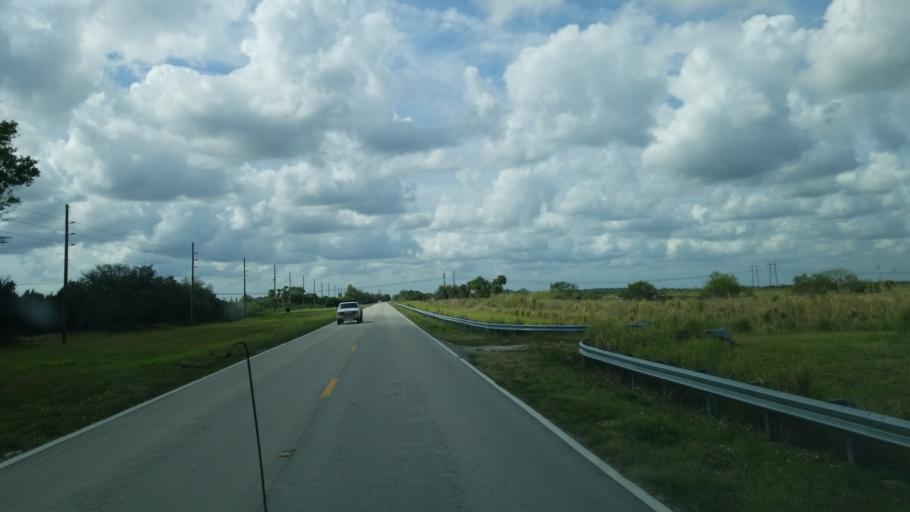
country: US
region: Florida
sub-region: Saint Lucie County
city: Lakewood Park
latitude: 27.4477
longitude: -80.5362
